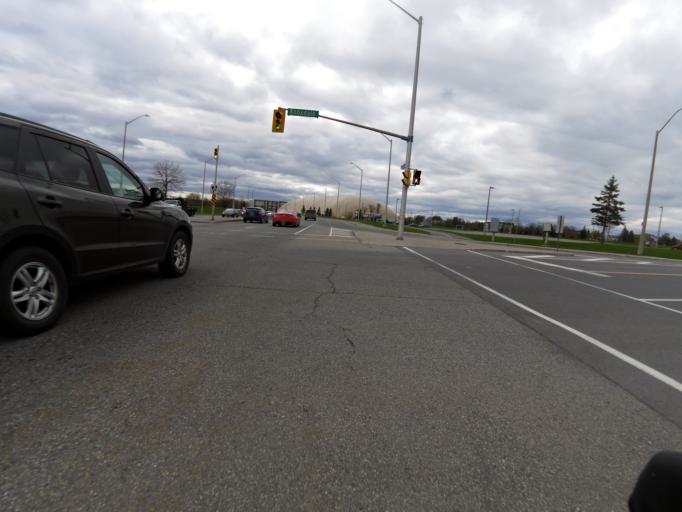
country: CA
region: Ontario
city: Bells Corners
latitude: 45.3229
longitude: -75.7720
